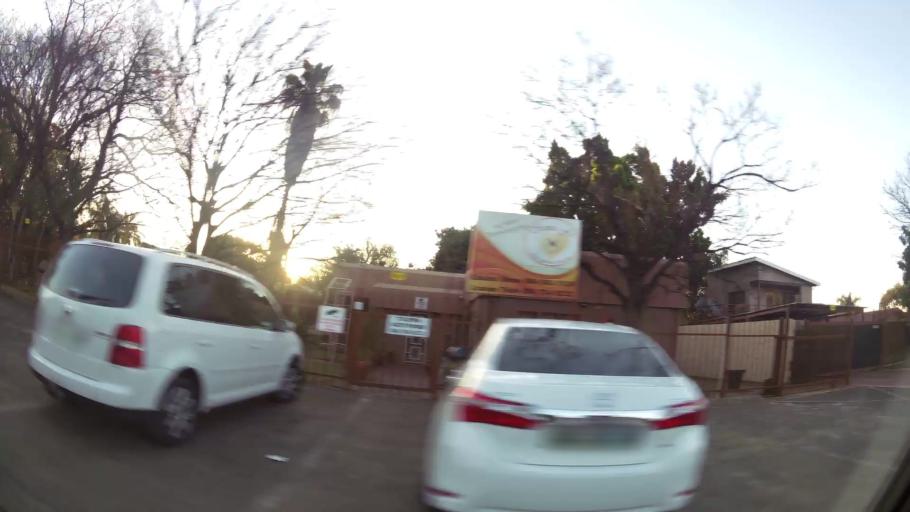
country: ZA
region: North-West
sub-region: Bojanala Platinum District Municipality
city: Rustenburg
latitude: -25.6761
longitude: 27.2220
